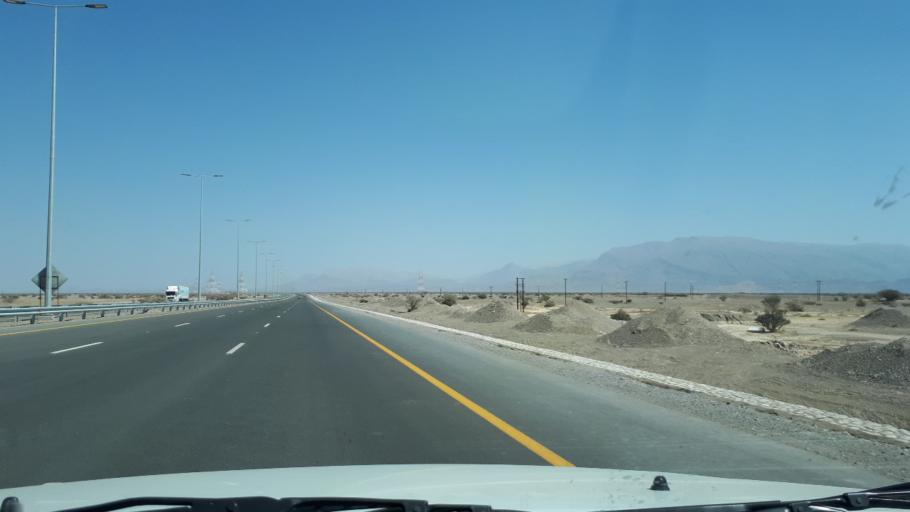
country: OM
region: Ash Sharqiyah
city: Badiyah
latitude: 22.2945
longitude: 59.1482
